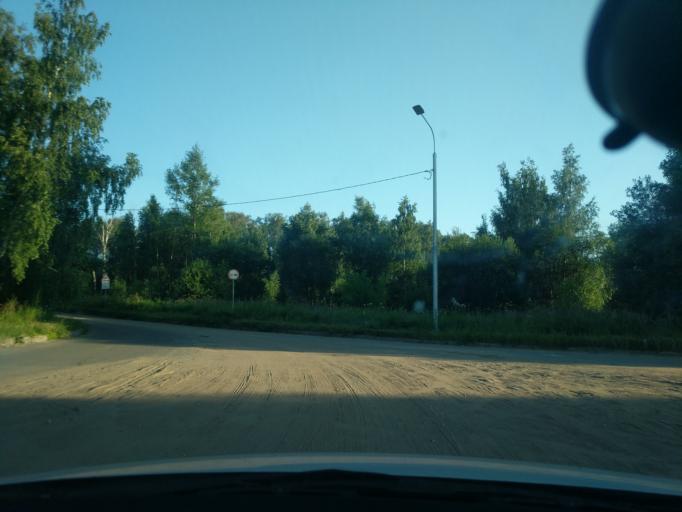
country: RU
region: Moskovskaya
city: Pushchino
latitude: 54.8432
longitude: 37.6407
